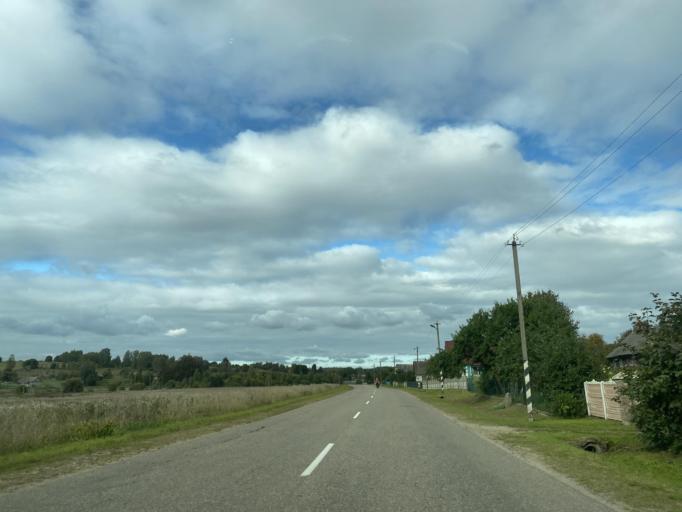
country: BY
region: Grodnenskaya
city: Kreva
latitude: 54.3000
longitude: 26.2761
